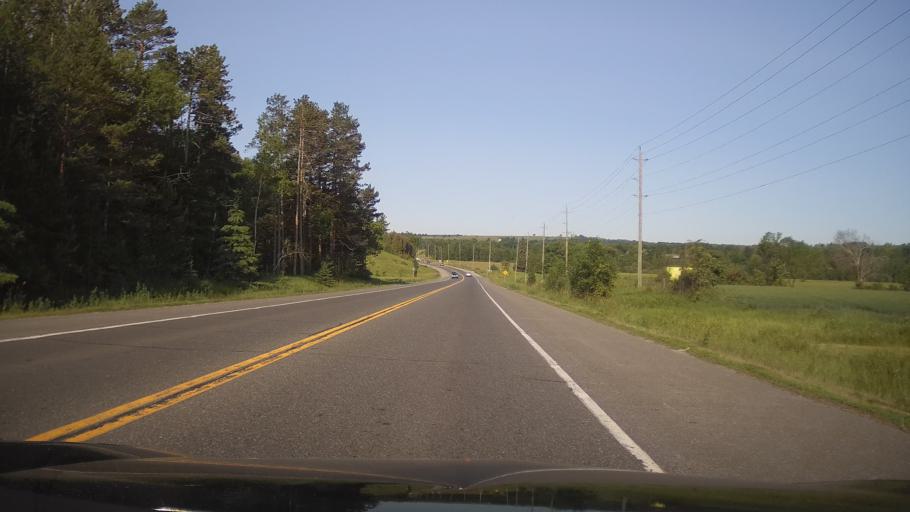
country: CA
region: Ontario
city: Peterborough
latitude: 44.3286
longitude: -78.1410
